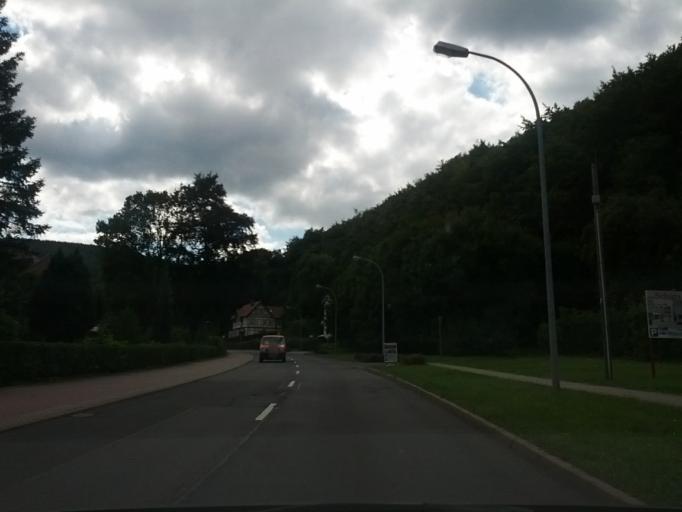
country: DE
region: Thuringia
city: Thal
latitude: 50.9173
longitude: 10.3905
